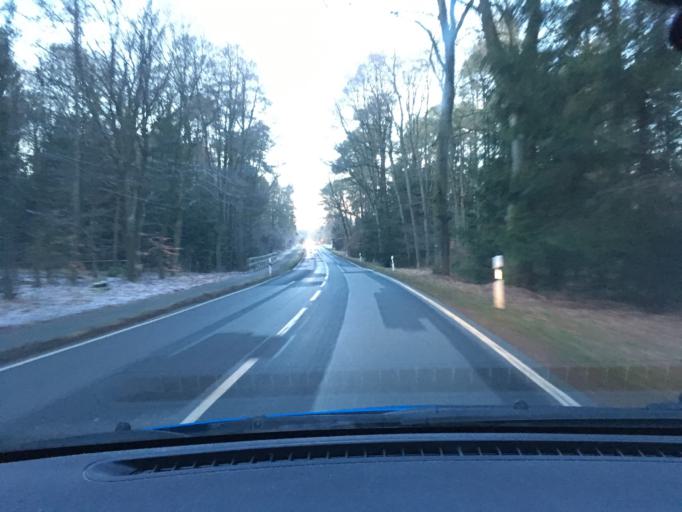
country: DE
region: Lower Saxony
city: Handeloh
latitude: 53.2739
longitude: 9.8786
